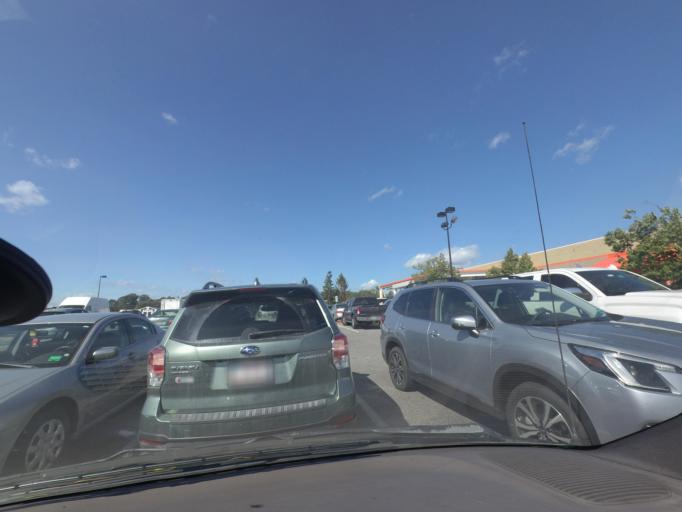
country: US
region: Maine
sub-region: Cumberland County
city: Westbrook
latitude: 43.6855
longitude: -70.3255
